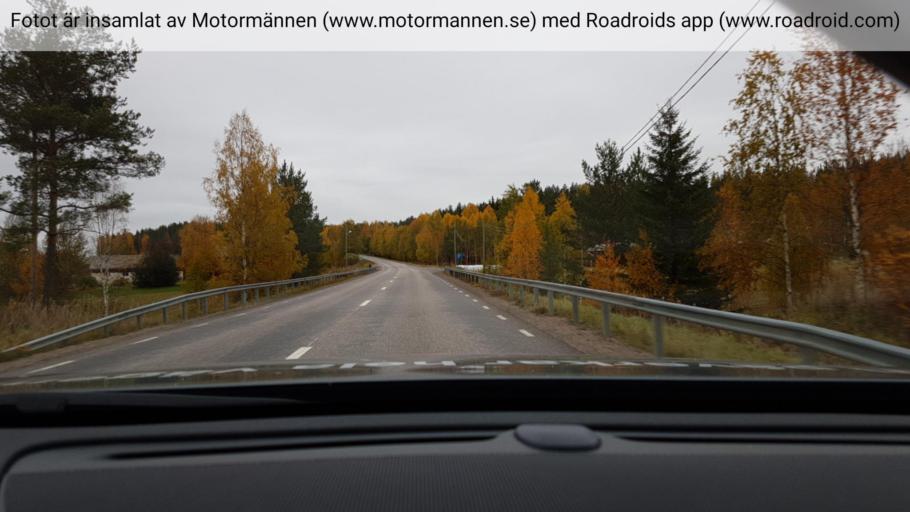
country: SE
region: Norrbotten
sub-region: Overkalix Kommun
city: OEverkalix
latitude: 66.5113
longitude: 22.7651
